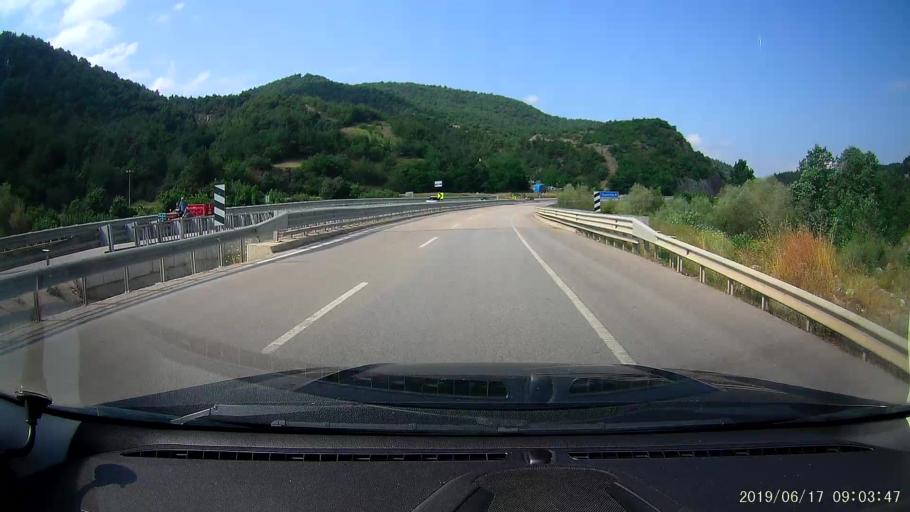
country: TR
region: Amasya
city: Tasova
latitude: 40.7504
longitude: 36.3014
